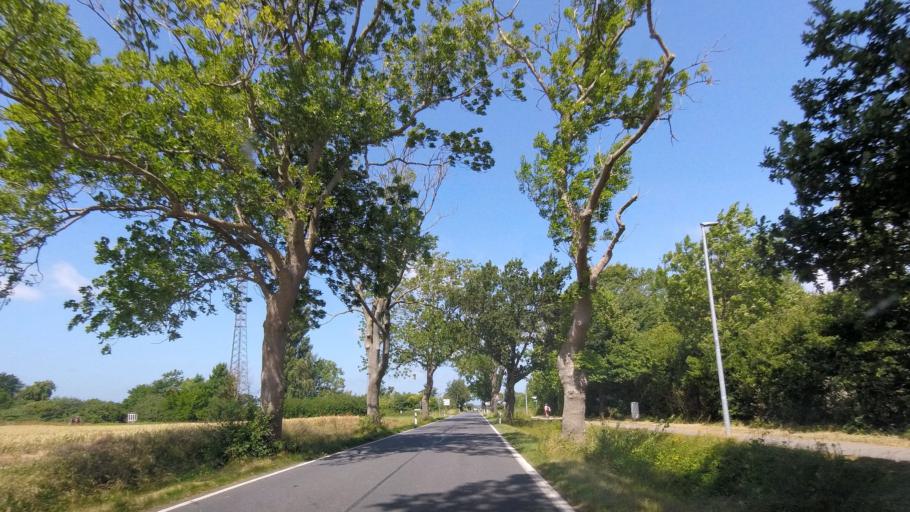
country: DE
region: Mecklenburg-Vorpommern
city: Wiek
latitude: 54.5501
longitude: 13.2451
